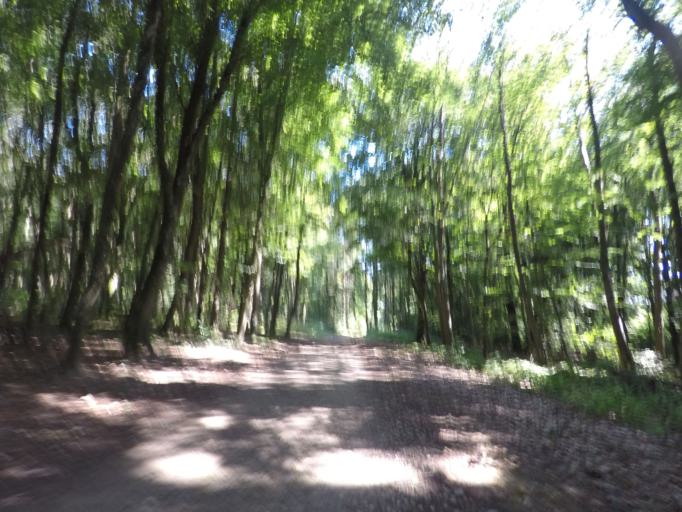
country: LU
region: Luxembourg
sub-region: Canton de Luxembourg
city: Strassen
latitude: 49.6319
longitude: 6.0774
